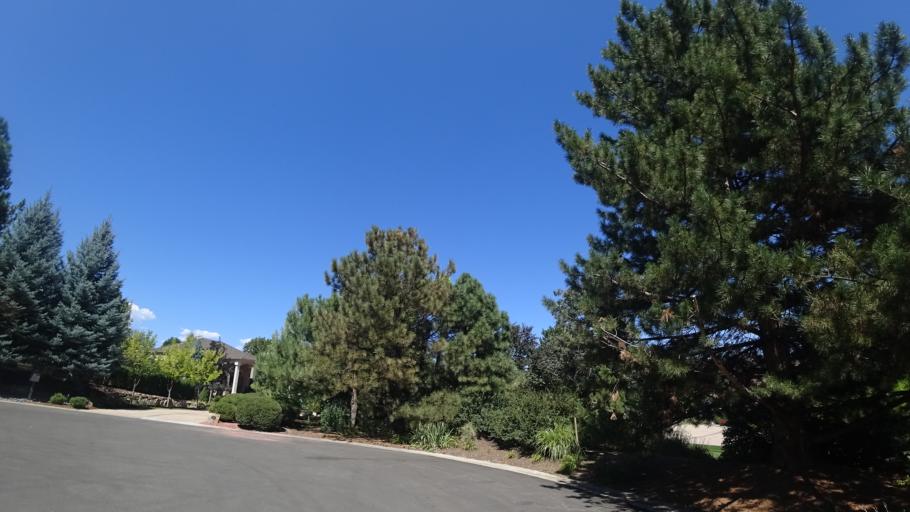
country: US
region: Colorado
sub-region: Arapahoe County
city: Greenwood Village
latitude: 39.6124
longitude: -104.9587
